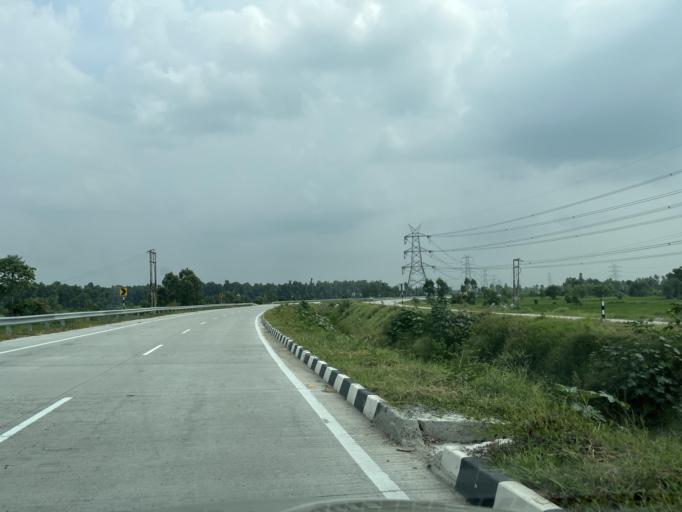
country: IN
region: Uttarakhand
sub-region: Udham Singh Nagar
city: Jaspur
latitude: 29.2801
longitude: 78.8663
